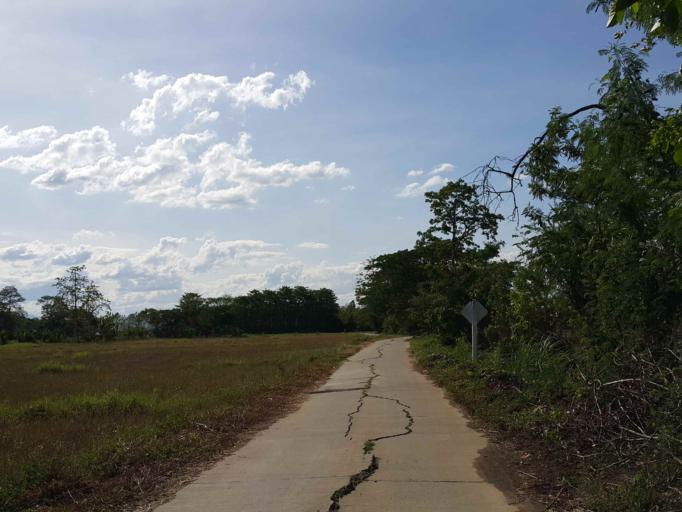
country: TH
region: Chiang Mai
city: San Kamphaeng
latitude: 18.7910
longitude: 99.1183
